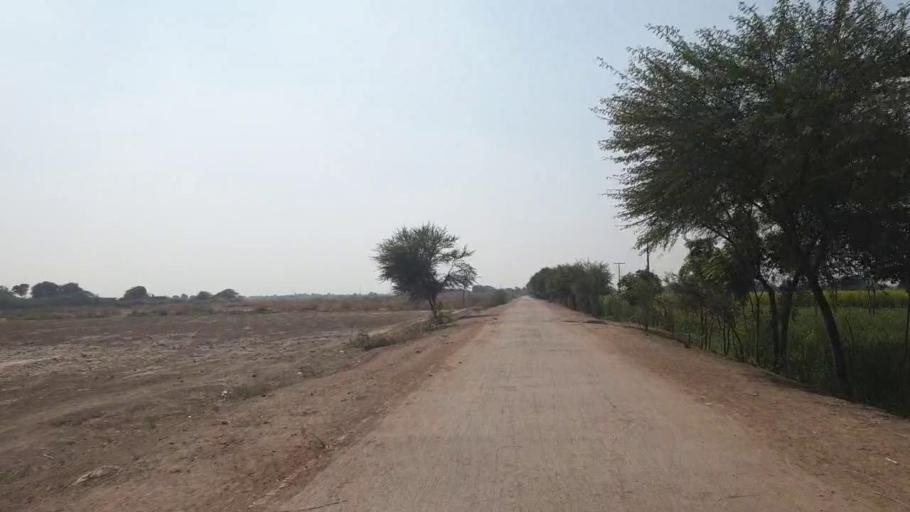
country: PK
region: Sindh
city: Chambar
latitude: 25.3878
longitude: 68.9244
